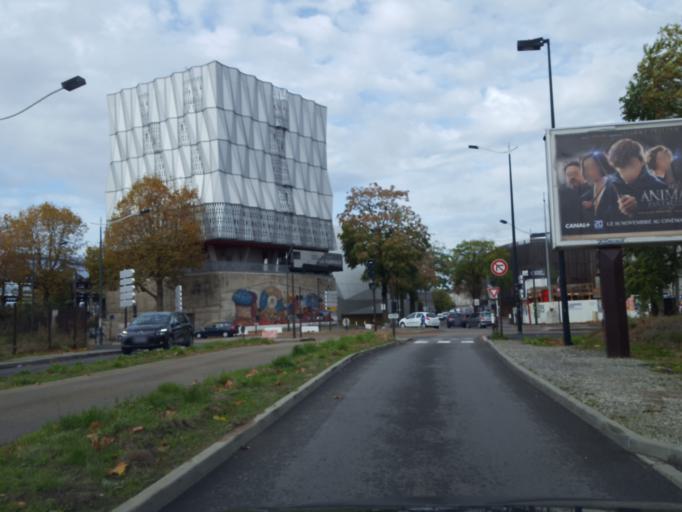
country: FR
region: Pays de la Loire
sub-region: Departement de la Loire-Atlantique
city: Nantes
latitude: 47.2041
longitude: -1.5619
